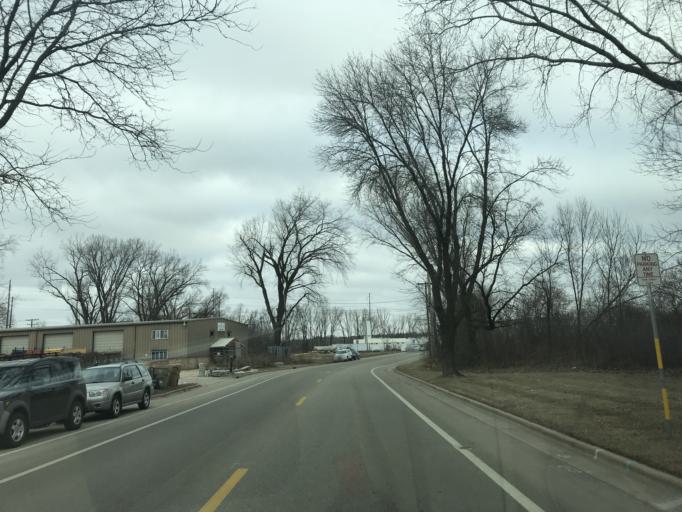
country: US
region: Wisconsin
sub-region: Dane County
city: Monona
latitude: 43.1118
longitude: -89.3100
